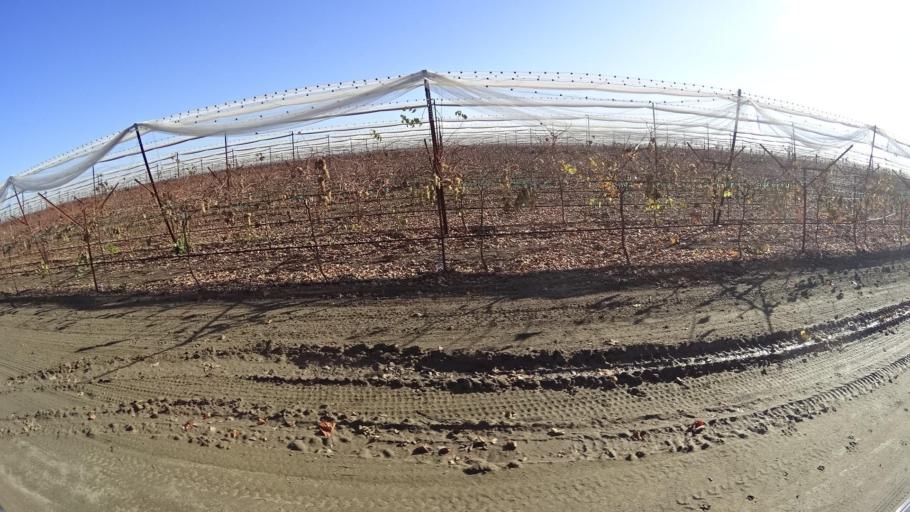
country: US
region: California
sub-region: Kern County
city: McFarland
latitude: 35.6985
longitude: -119.2674
